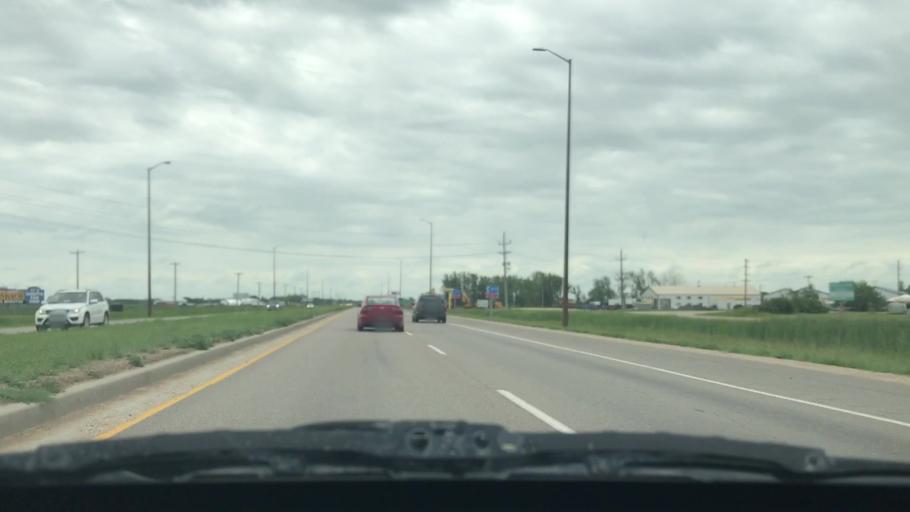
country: CA
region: Manitoba
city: Winnipeg
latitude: 49.8527
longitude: -97.0051
